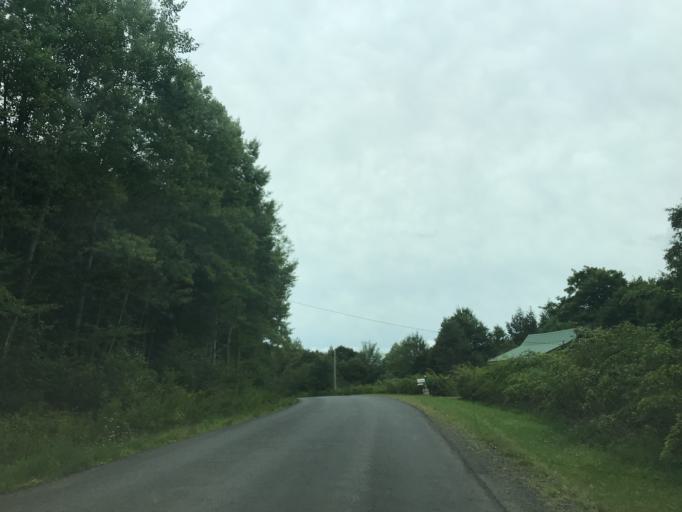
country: US
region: New York
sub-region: Otsego County
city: Worcester
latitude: 42.5913
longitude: -74.6807
